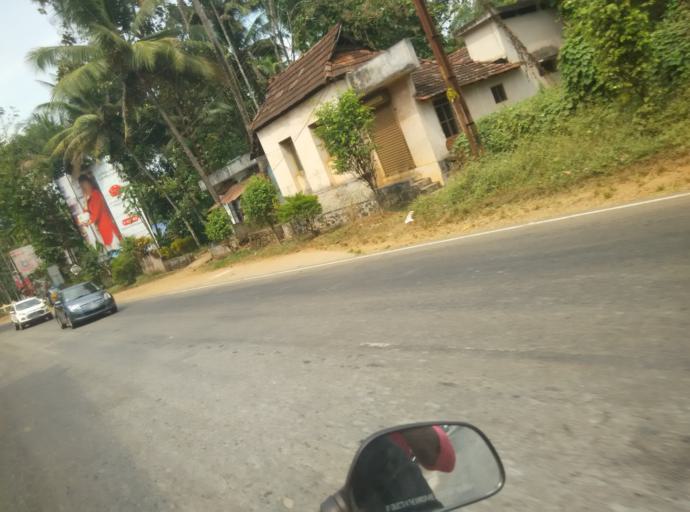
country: IN
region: Kerala
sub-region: Kottayam
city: Palackattumala
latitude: 9.6985
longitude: 76.6510
